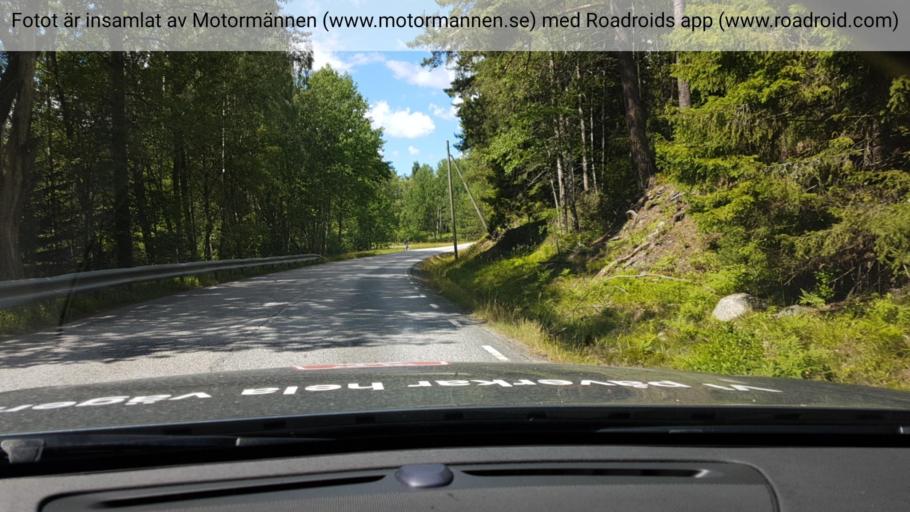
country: SE
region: Stockholm
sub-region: Varmdo Kommun
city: Hemmesta
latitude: 59.3909
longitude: 18.4962
